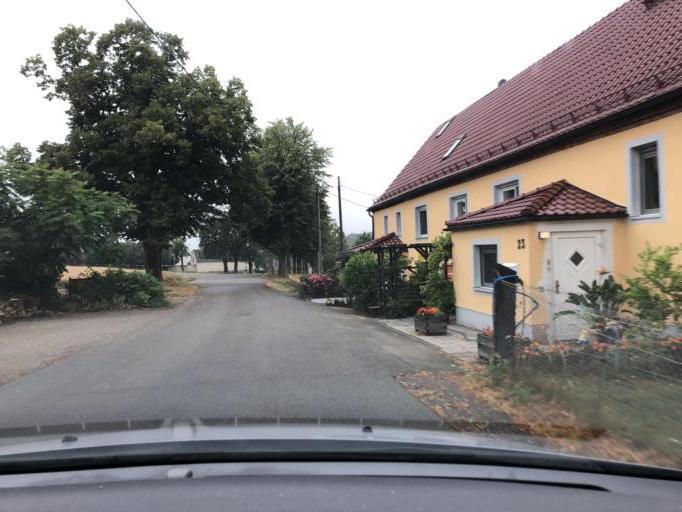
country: DE
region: Thuringia
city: Langenleuba-Niederhain
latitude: 50.9946
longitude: 12.6446
